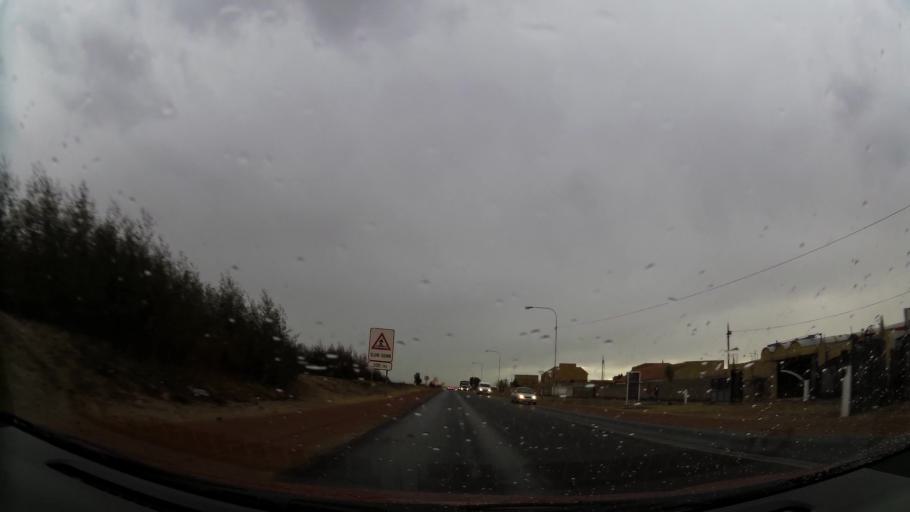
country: ZA
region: Gauteng
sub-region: City of Johannesburg Metropolitan Municipality
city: Roodepoort
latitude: -26.1730
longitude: 27.8002
